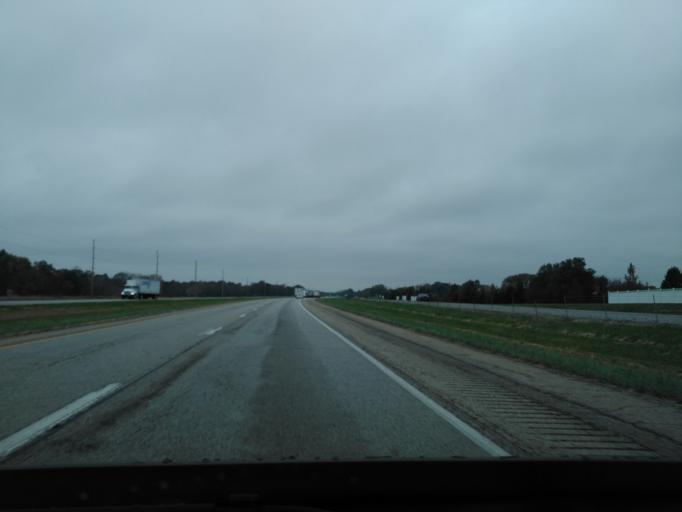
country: US
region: Illinois
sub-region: Bond County
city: Greenville
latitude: 38.8478
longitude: -89.4702
